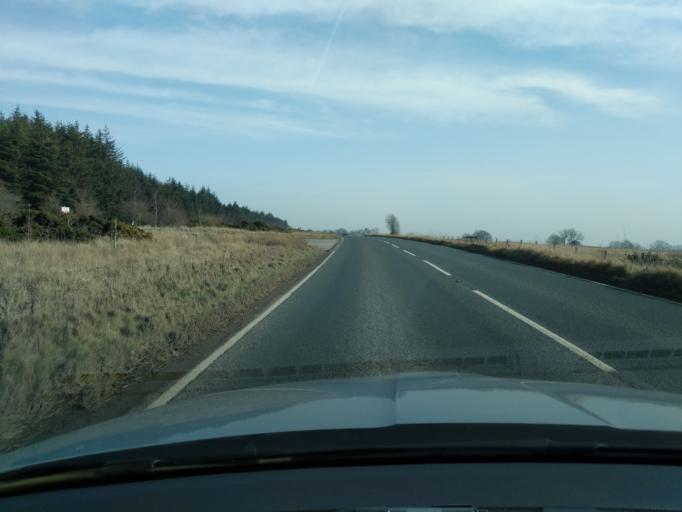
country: GB
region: England
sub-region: North Yorkshire
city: Leyburn
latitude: 54.3489
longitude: -1.7898
